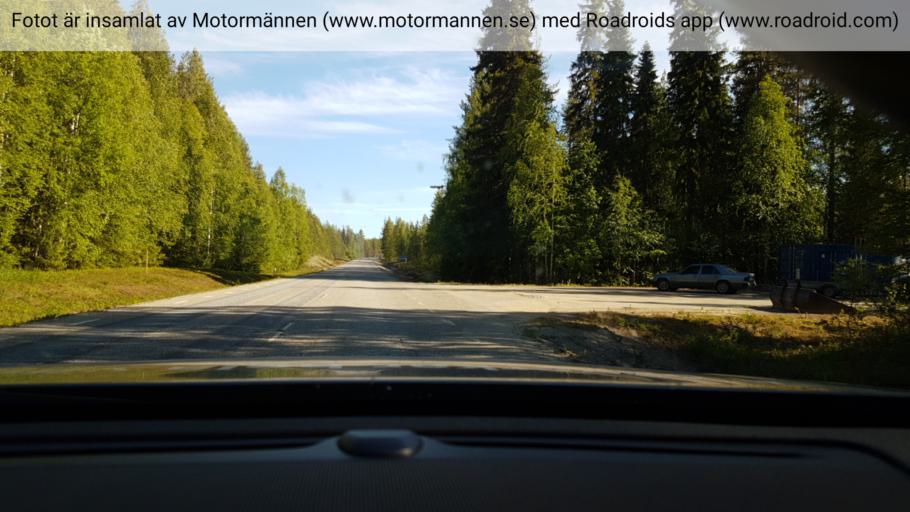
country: SE
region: Vaesterbotten
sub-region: Norsjo Kommun
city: Norsjoe
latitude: 64.6092
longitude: 19.2947
